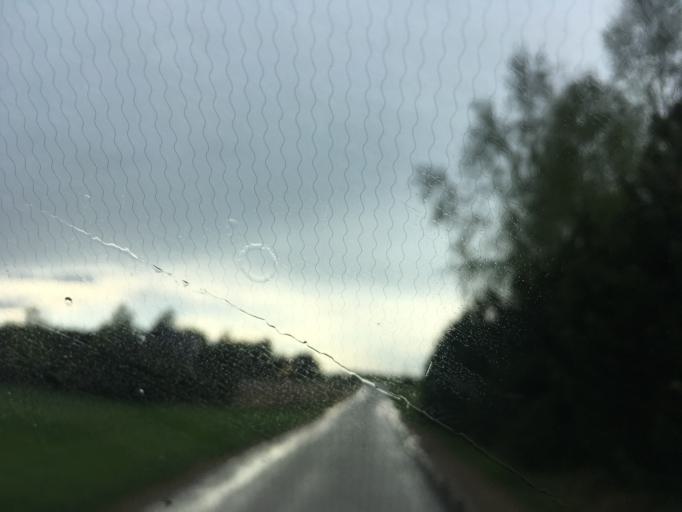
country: PL
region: Warmian-Masurian Voivodeship
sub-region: Powiat dzialdowski
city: Rybno
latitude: 53.3814
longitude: 19.9615
